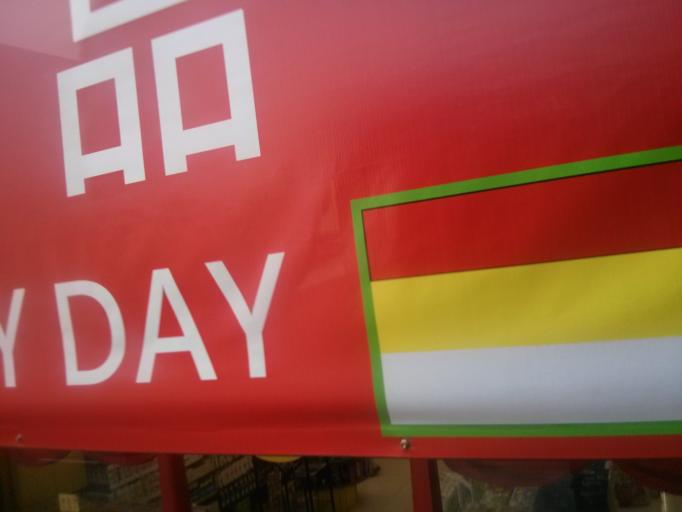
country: SG
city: Singapore
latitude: 1.3096
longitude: 103.8575
